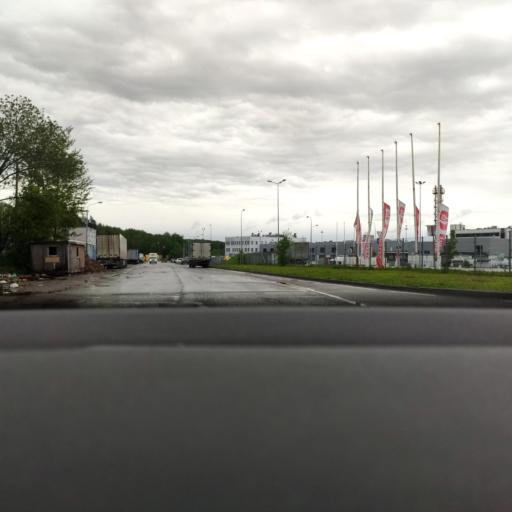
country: RU
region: Moscow
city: Lianozovo
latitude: 55.9167
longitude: 37.5872
